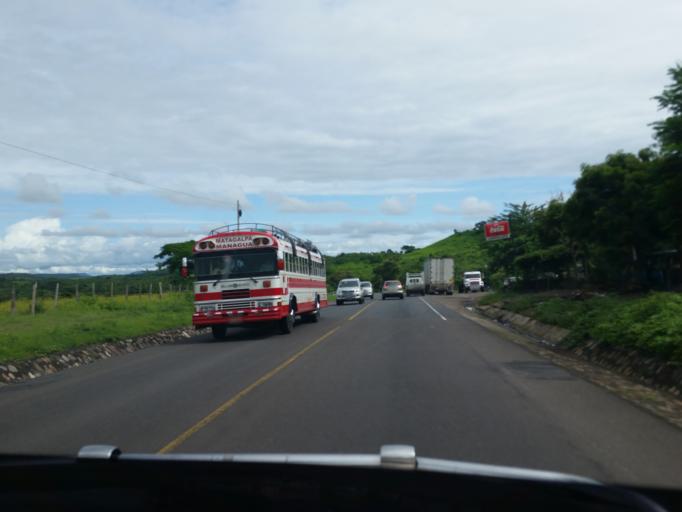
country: NI
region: Matagalpa
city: Ciudad Dario
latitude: 12.5272
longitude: -86.0502
